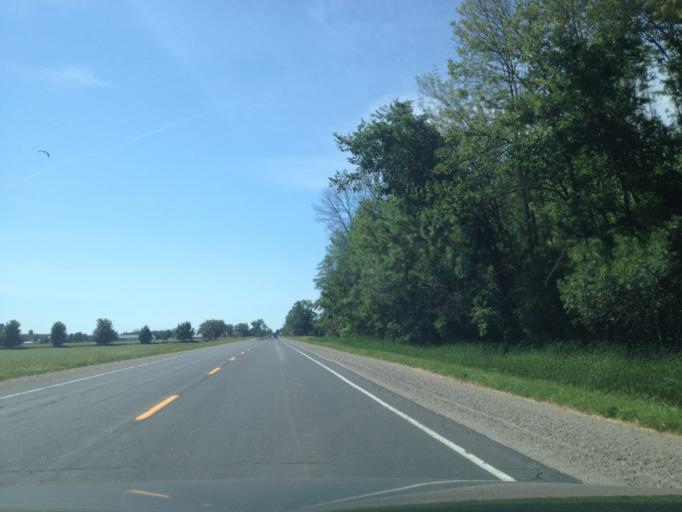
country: CA
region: Ontario
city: Stratford
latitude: 43.4951
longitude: -80.8618
